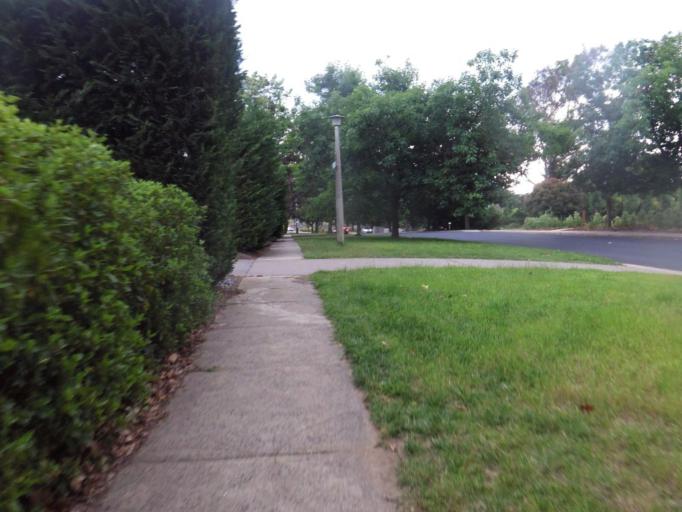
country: AU
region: Australian Capital Territory
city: Forrest
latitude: -35.3384
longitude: 149.1235
